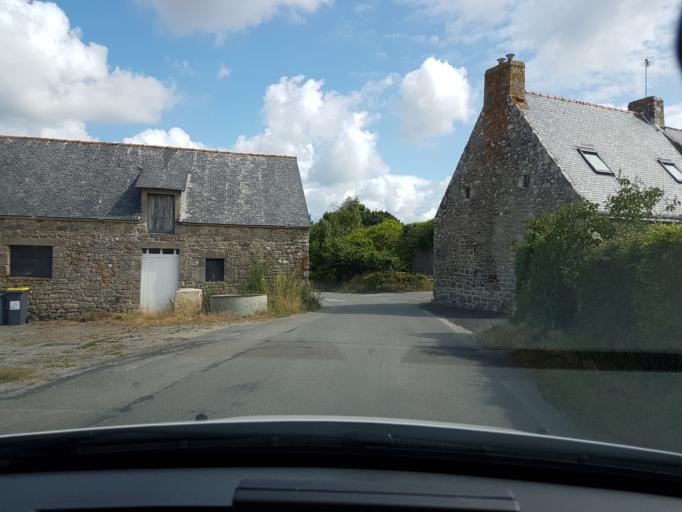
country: FR
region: Brittany
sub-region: Departement du Morbihan
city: Sainte-Helene
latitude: 47.7080
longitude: -3.1935
